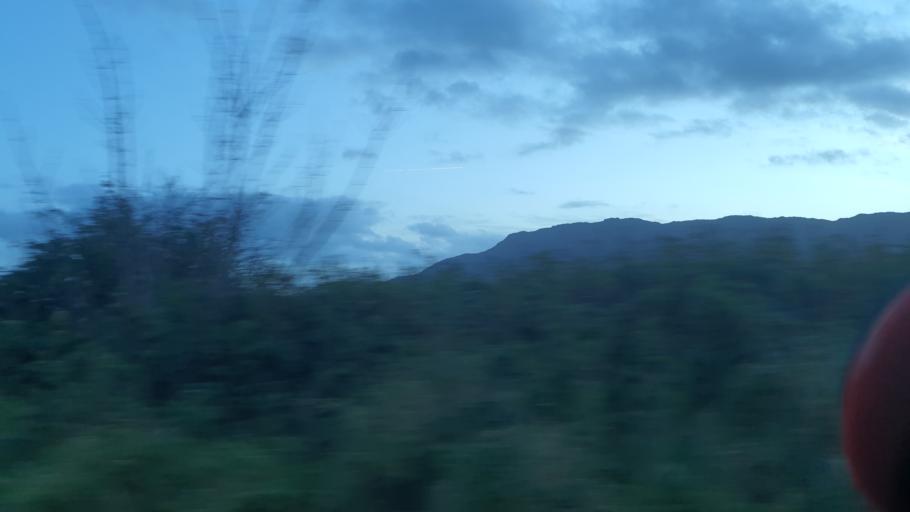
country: GB
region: Northern Ireland
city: Rostrevor
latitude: 54.0747
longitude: -6.1779
